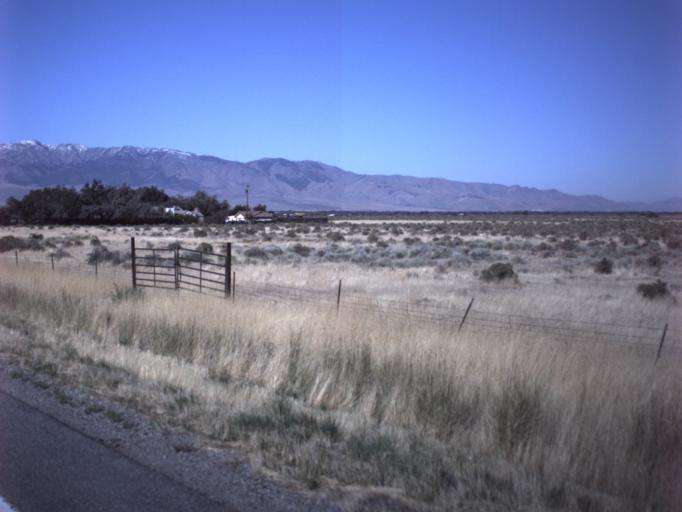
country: US
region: Utah
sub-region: Tooele County
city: Grantsville
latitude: 40.6056
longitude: -112.3896
